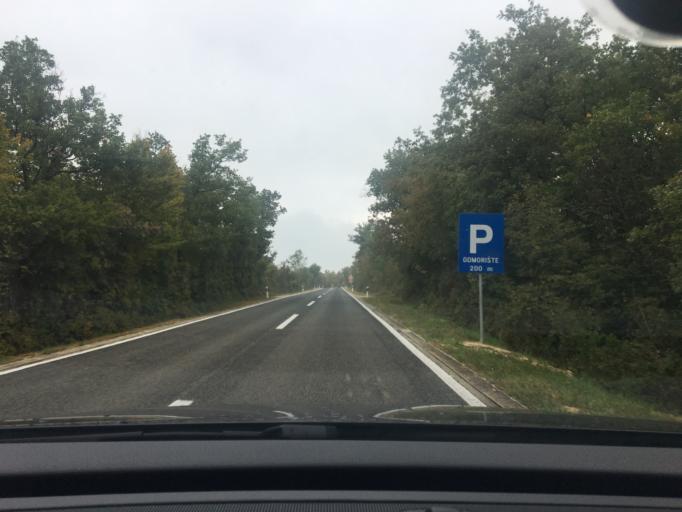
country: HR
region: Istarska
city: Buje
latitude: 45.4313
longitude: 13.6575
